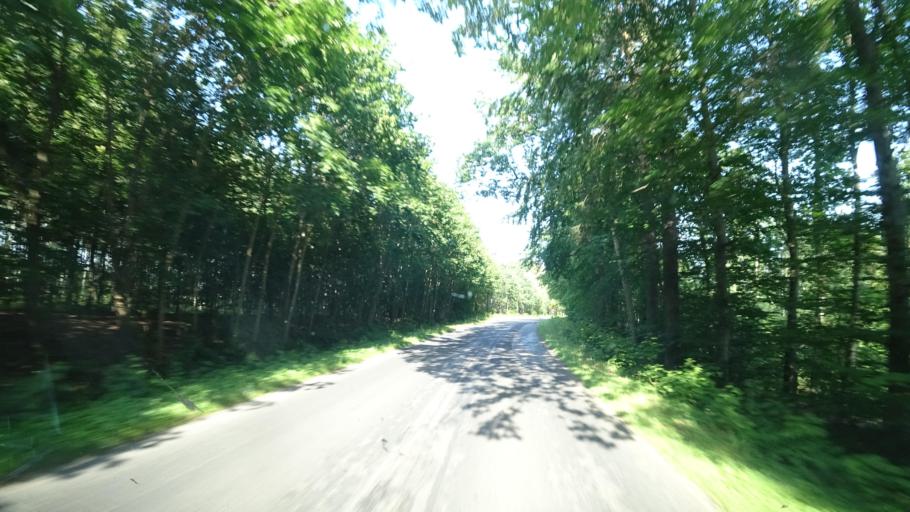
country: PL
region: Pomeranian Voivodeship
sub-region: Powiat czluchowski
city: Przechlewo
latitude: 53.7954
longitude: 17.1918
